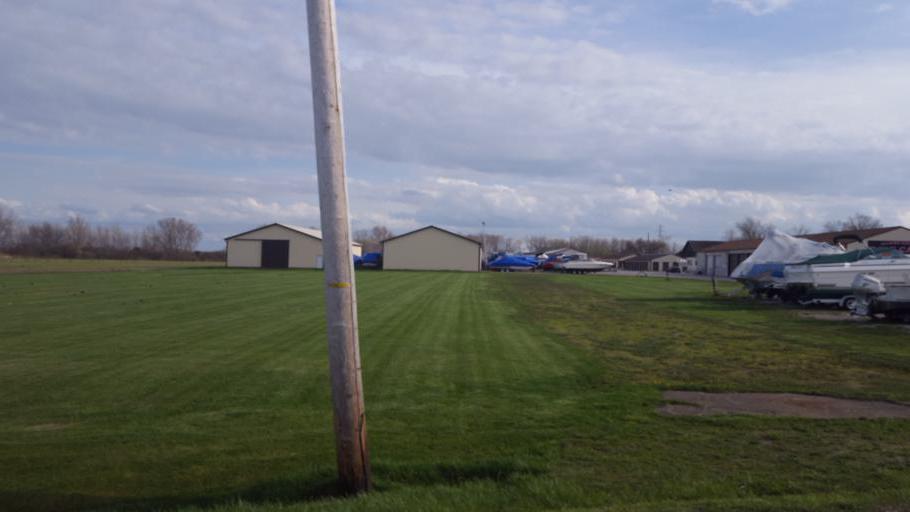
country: US
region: Ohio
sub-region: Ottawa County
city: Port Clinton
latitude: 41.5037
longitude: -82.8266
